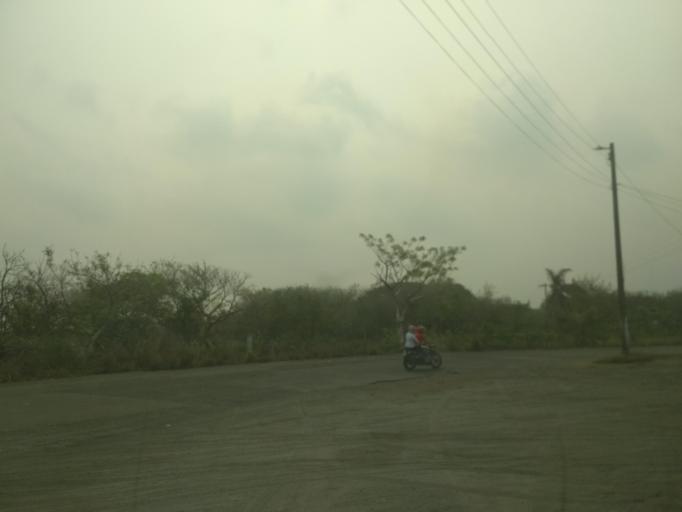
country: MX
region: Veracruz
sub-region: Veracruz
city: Delfino Victoria (Santa Fe)
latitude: 19.2086
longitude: -96.2618
